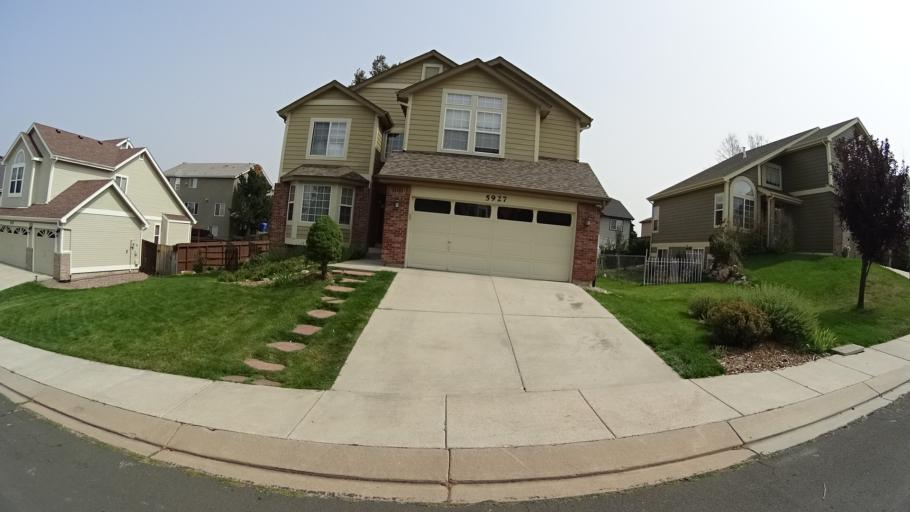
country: US
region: Colorado
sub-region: El Paso County
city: Cimarron Hills
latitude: 38.9158
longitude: -104.7492
